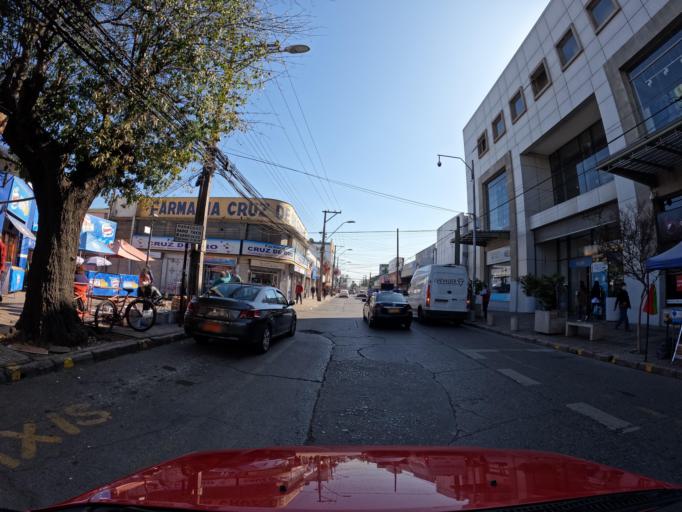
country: CL
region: Maule
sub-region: Provincia de Curico
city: Curico
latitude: -34.9823
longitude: -71.2418
